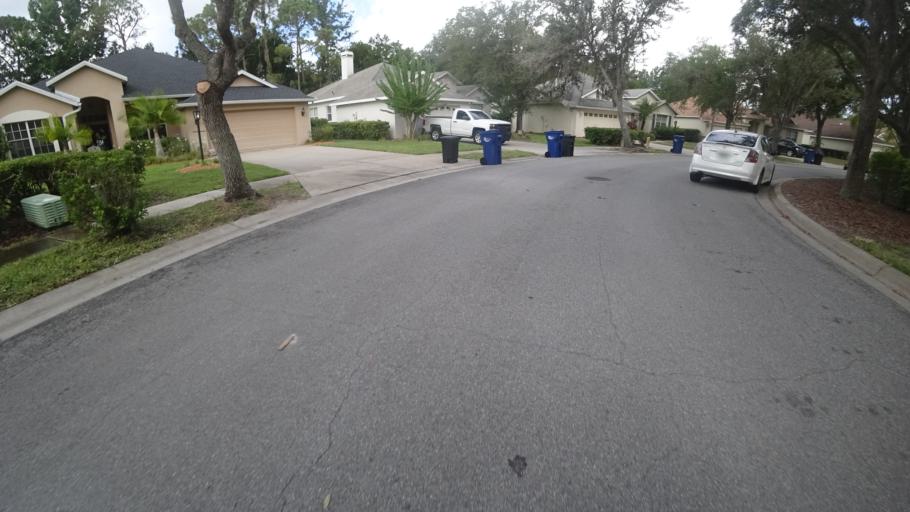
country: US
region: Florida
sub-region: Sarasota County
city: The Meadows
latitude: 27.4215
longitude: -82.4299
